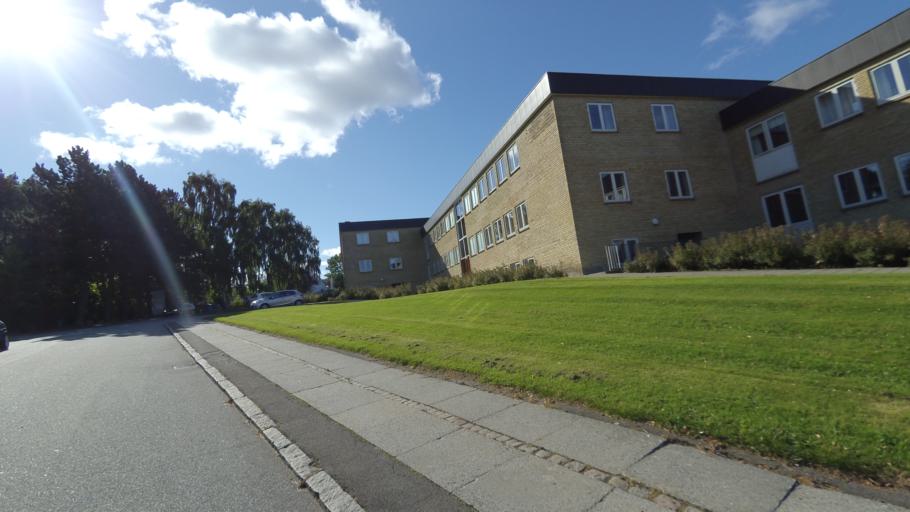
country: DK
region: Central Jutland
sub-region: Arhus Kommune
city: Stavtrup
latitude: 56.1249
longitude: 10.1640
